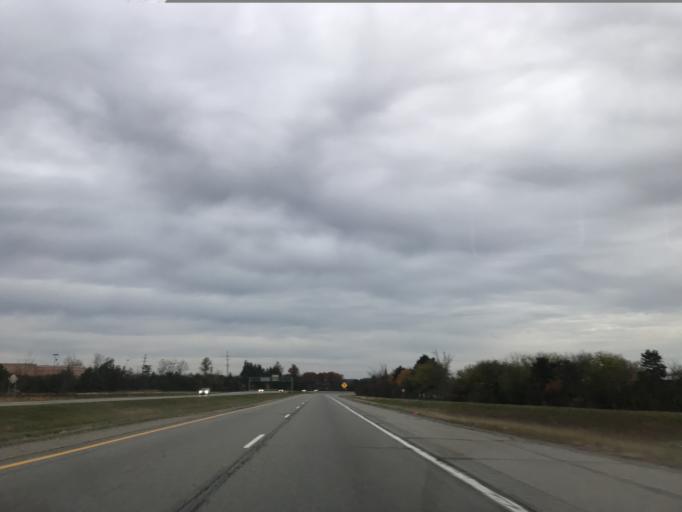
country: US
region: Michigan
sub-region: Washtenaw County
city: Ann Arbor
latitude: 42.2554
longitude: -83.6837
